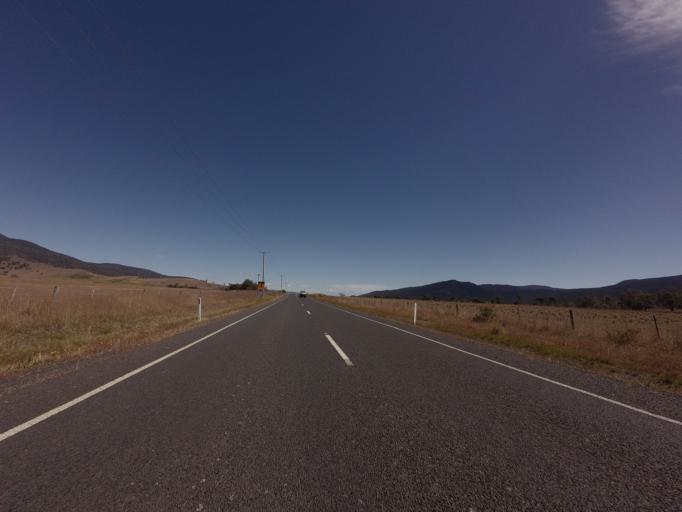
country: AU
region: Tasmania
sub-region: Break O'Day
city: St Helens
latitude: -41.7113
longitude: 147.8410
